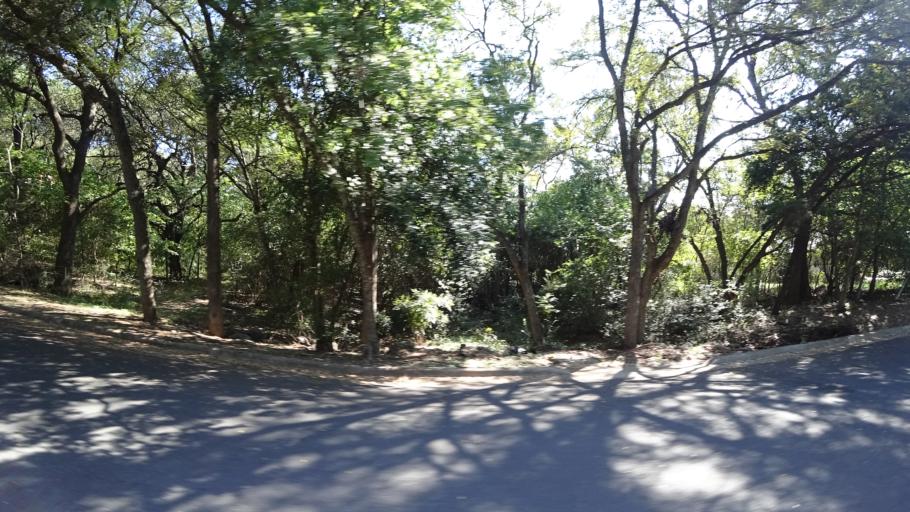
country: US
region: Texas
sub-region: Travis County
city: Rollingwood
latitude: 30.2715
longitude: -97.8091
